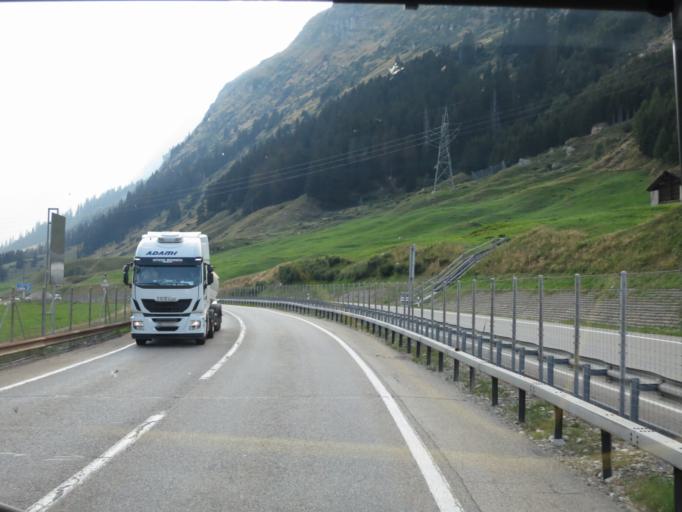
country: CH
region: Grisons
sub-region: Hinterrhein District
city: Hinterrhein
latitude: 46.5303
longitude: 9.1956
